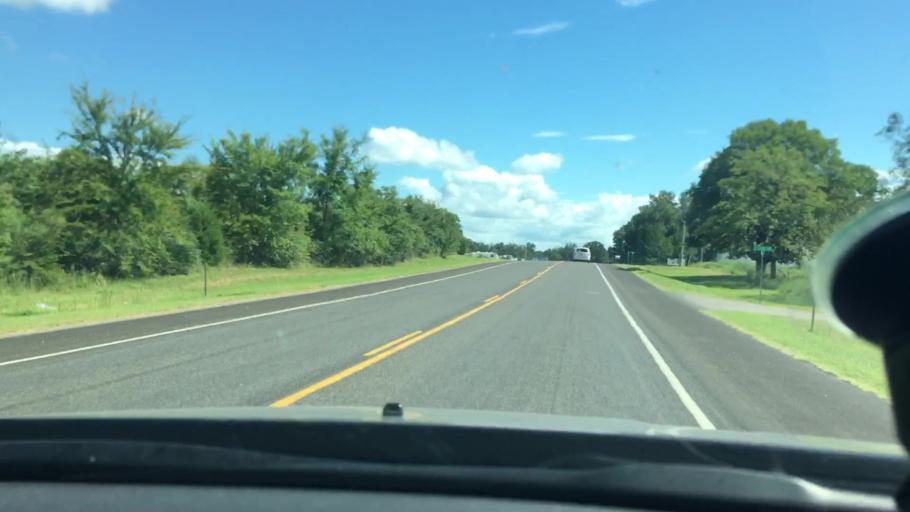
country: US
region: Oklahoma
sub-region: Sequoyah County
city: Vian
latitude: 35.5599
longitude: -94.9809
